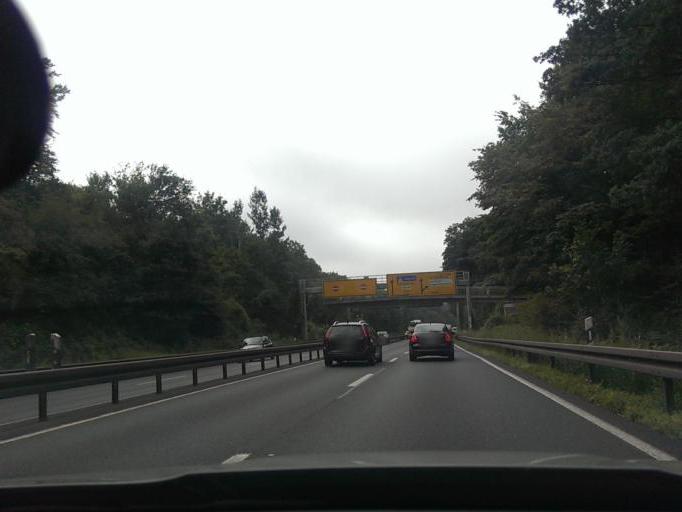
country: DE
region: Lower Saxony
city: Hannover
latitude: 52.3856
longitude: 9.7850
